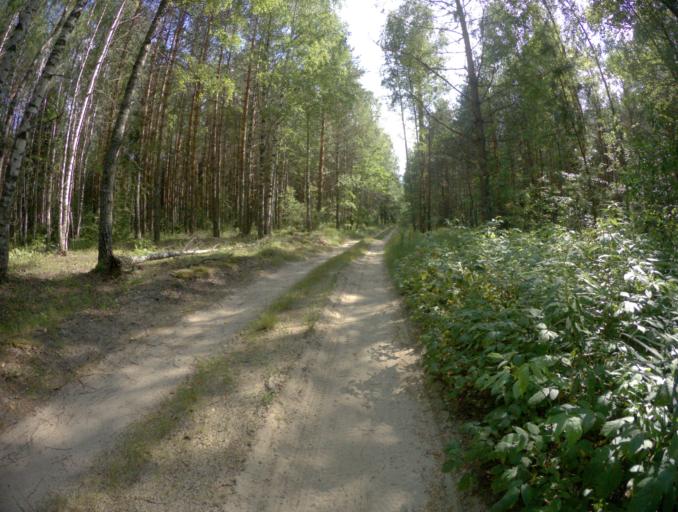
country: RU
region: Vladimir
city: Vorsha
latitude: 55.9385
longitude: 40.1449
